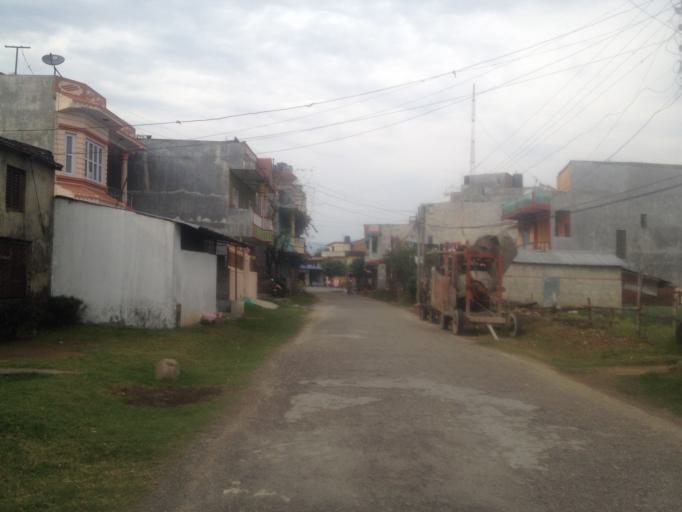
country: NP
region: Central Region
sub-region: Narayani Zone
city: Bharatpur
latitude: 27.6896
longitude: 84.4361
